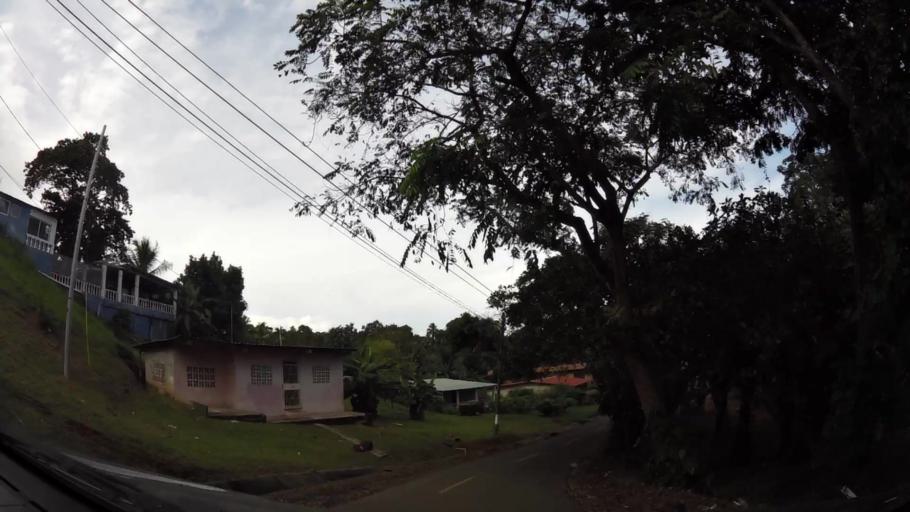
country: PA
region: Panama
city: El Coco
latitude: 8.8678
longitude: -79.8125
